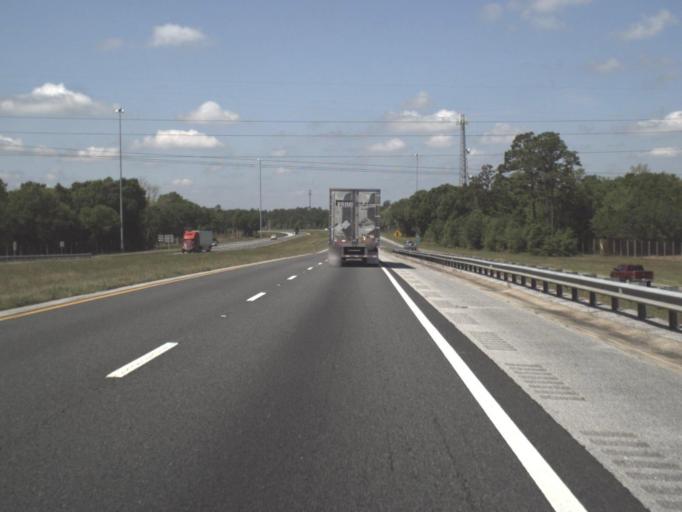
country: US
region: Florida
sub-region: Santa Rosa County
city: East Milton
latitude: 30.6184
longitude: -86.9650
